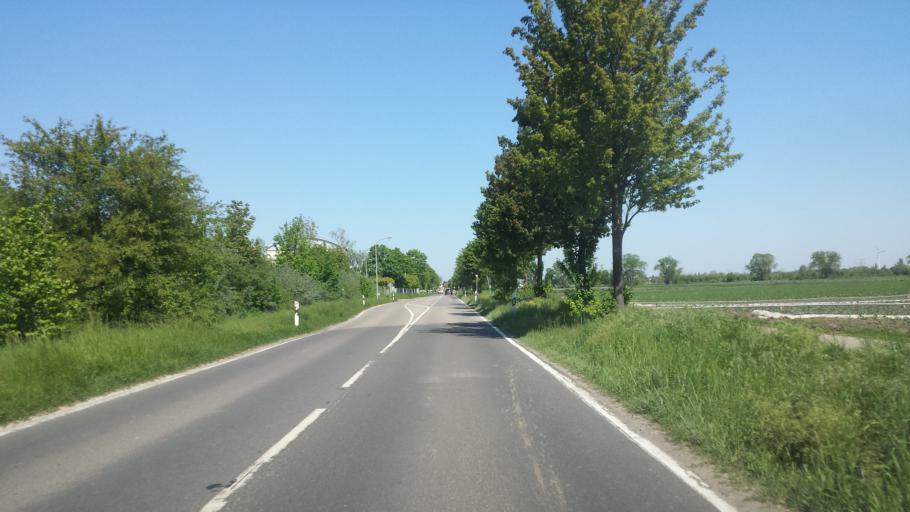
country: DE
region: Rheinland-Pfalz
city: Maxdorf
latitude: 49.4900
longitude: 8.2949
